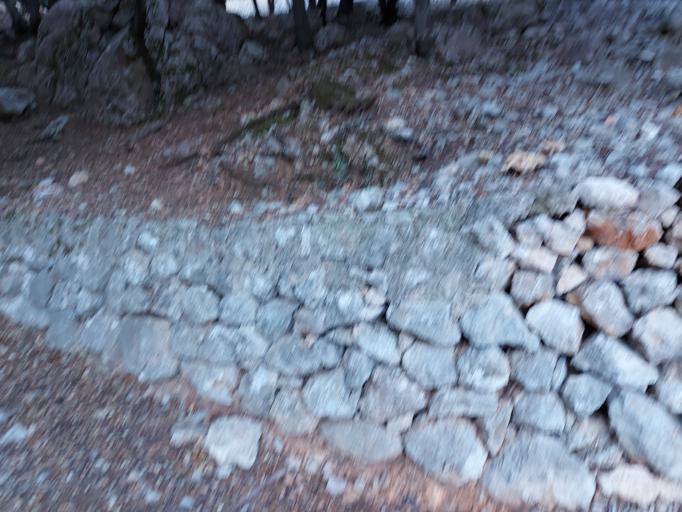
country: ES
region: Balearic Islands
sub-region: Illes Balears
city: Deia
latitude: 39.7258
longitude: 2.6528
